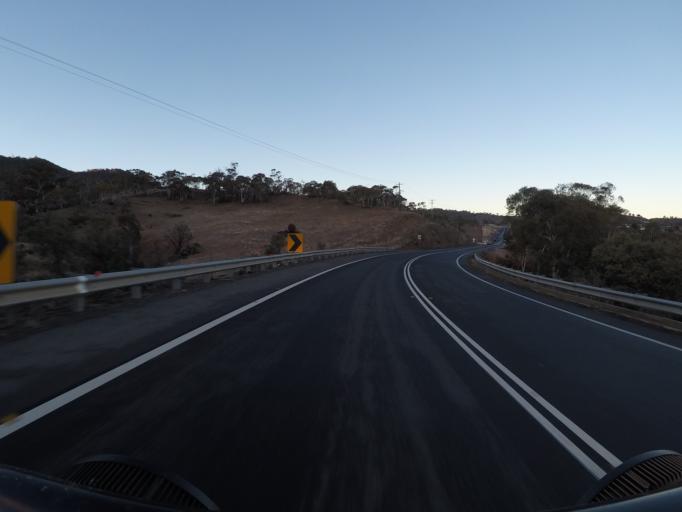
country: AU
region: New South Wales
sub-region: Snowy River
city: Jindabyne
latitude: -36.3992
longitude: 148.6537
